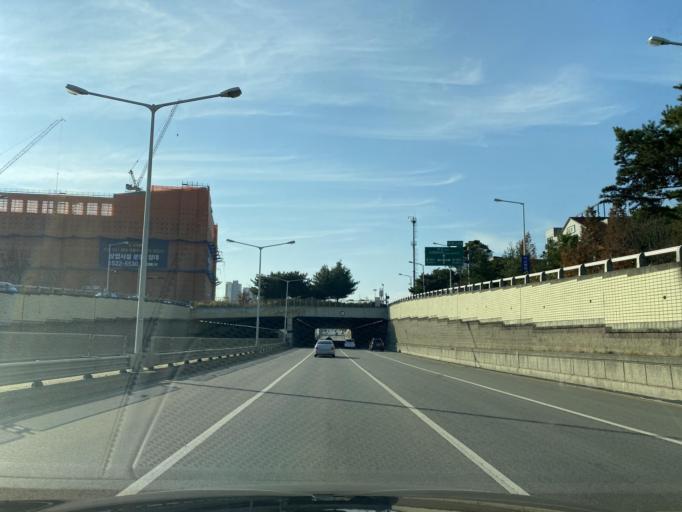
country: KR
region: Chungcheongnam-do
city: Cheonan
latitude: 36.7845
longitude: 127.1117
